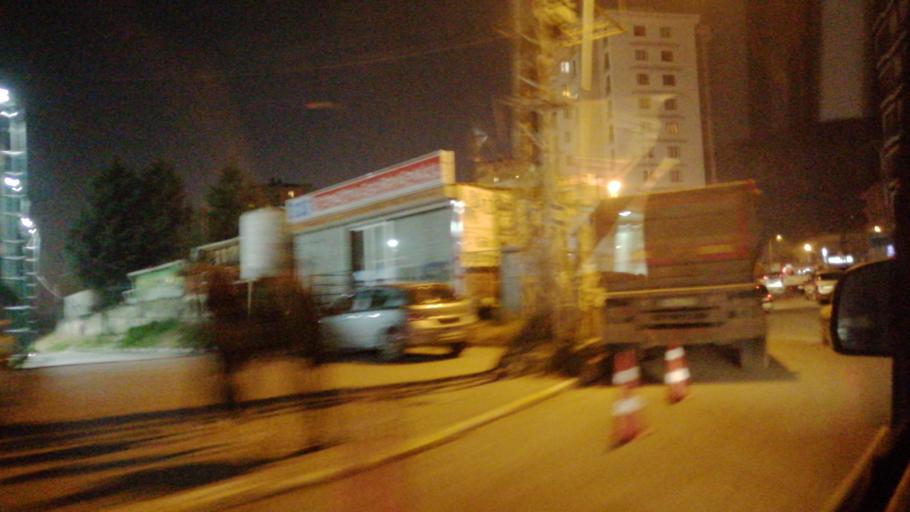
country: TR
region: Istanbul
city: Umraniye
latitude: 41.0175
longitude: 29.1287
